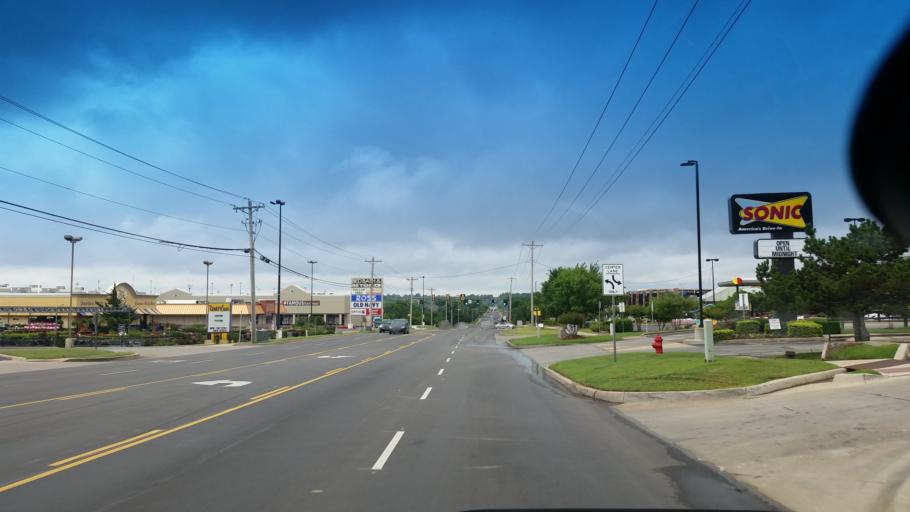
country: US
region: Oklahoma
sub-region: Oklahoma County
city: Edmond
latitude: 35.6515
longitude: -97.4605
